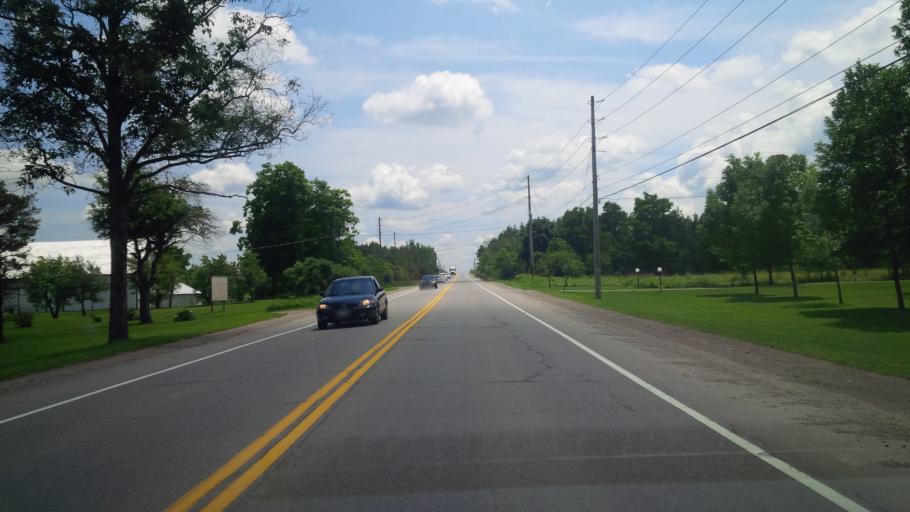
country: CA
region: Ontario
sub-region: Wellington County
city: Guelph
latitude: 43.4921
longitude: -80.1779
